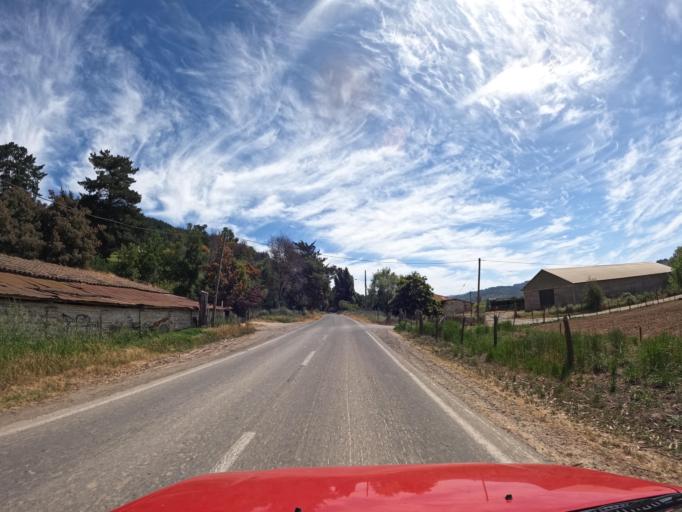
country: CL
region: Maule
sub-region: Provincia de Talca
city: Talca
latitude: -34.9894
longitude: -71.8209
